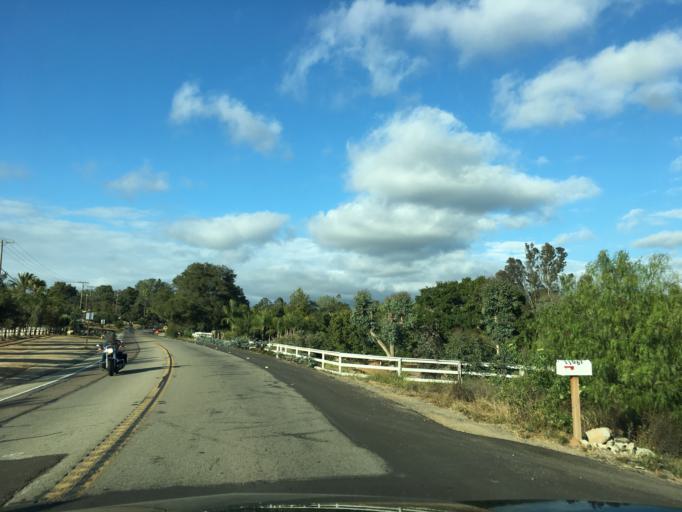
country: US
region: California
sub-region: San Diego County
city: Hidden Meadows
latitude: 33.2542
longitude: -117.0925
